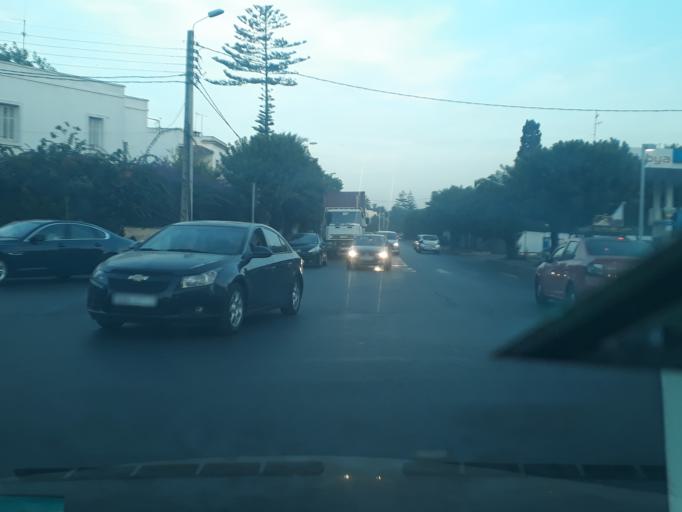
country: MA
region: Grand Casablanca
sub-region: Casablanca
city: Casablanca
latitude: 33.5845
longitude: -7.6503
